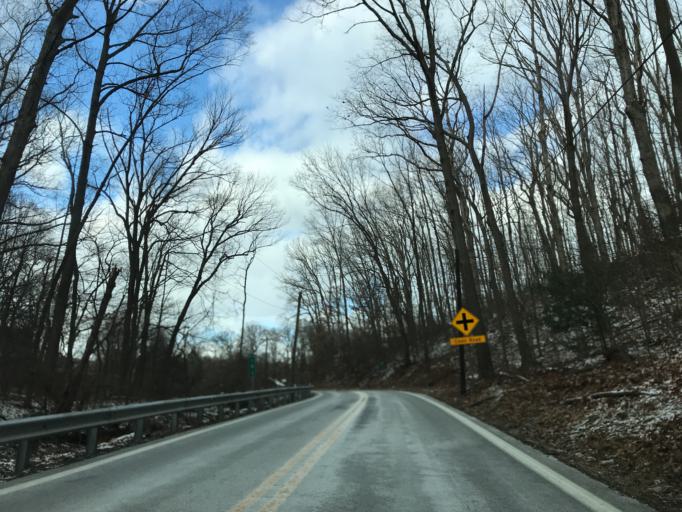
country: US
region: Maryland
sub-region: Harford County
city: Jarrettsville
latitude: 39.6486
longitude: -76.4104
